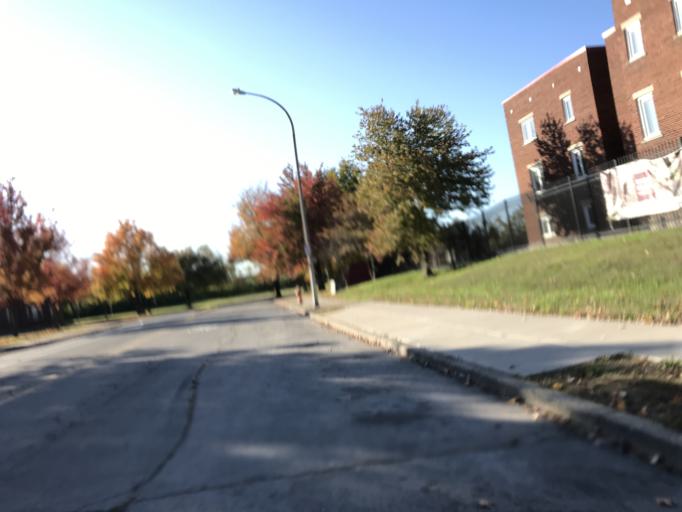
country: US
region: Kentucky
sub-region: Jefferson County
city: Louisville
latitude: 38.2248
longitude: -85.7644
